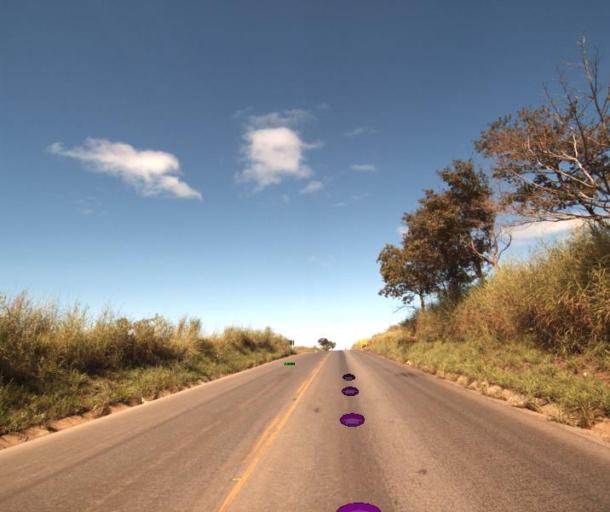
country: BR
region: Goias
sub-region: Itapaci
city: Itapaci
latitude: -15.0976
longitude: -49.4755
